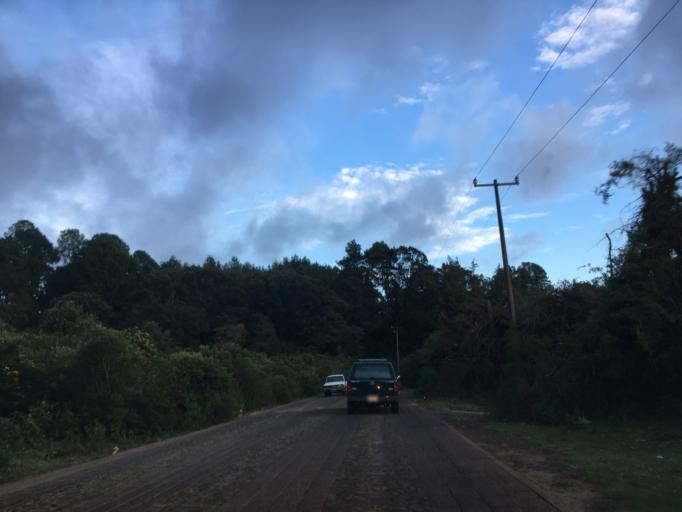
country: MX
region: Michoacan
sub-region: Patzcuaro
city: Santa Maria Huiramangaro (San Juan Tumbio)
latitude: 19.4406
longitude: -101.7220
